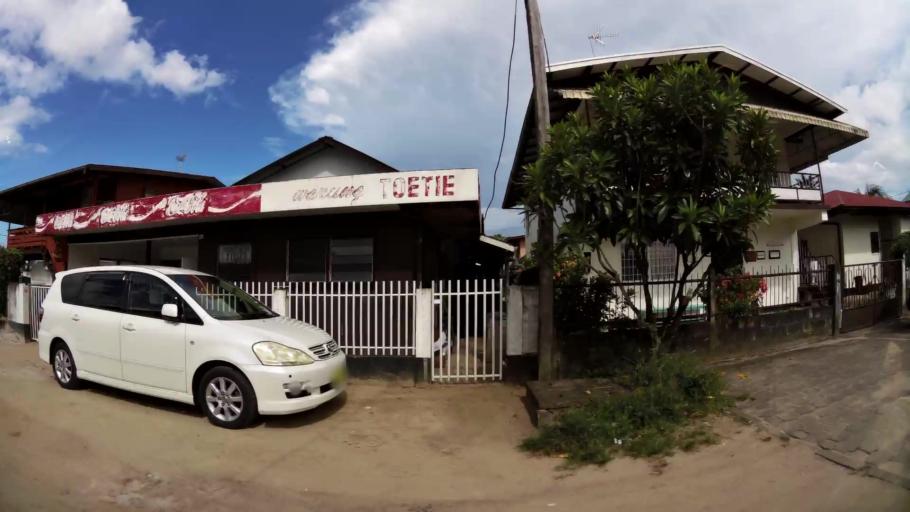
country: SR
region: Paramaribo
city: Paramaribo
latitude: 5.8450
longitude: -55.1483
